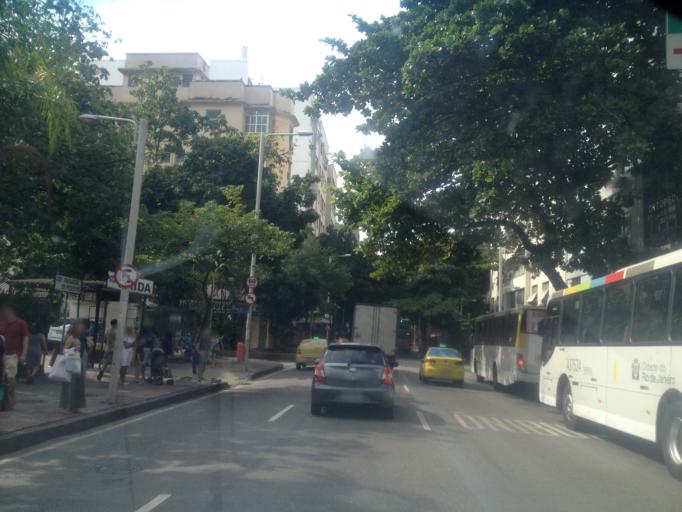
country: BR
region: Rio de Janeiro
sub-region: Rio De Janeiro
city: Rio de Janeiro
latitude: -22.9557
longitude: -43.1966
